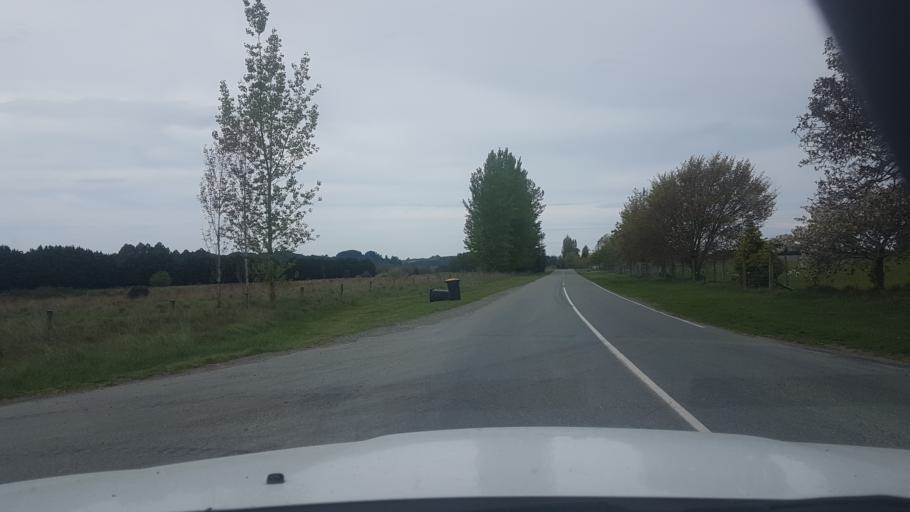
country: NZ
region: Canterbury
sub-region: Timaru District
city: Pleasant Point
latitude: -44.0750
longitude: 171.1705
